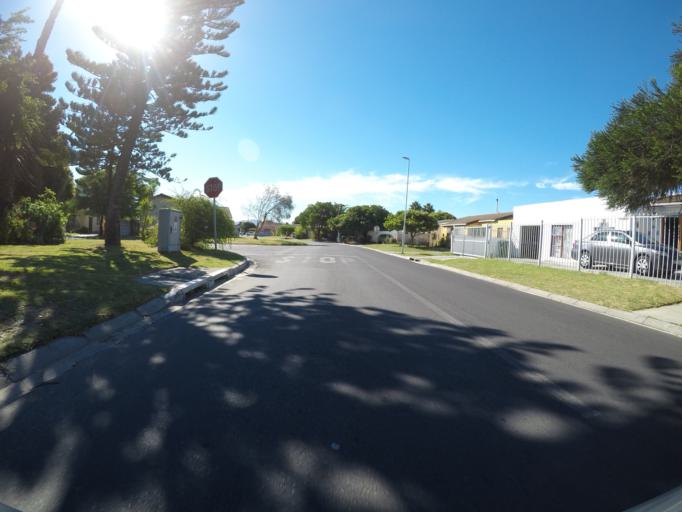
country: ZA
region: Western Cape
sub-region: City of Cape Town
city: Kraaifontein
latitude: -33.9442
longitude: 18.6851
